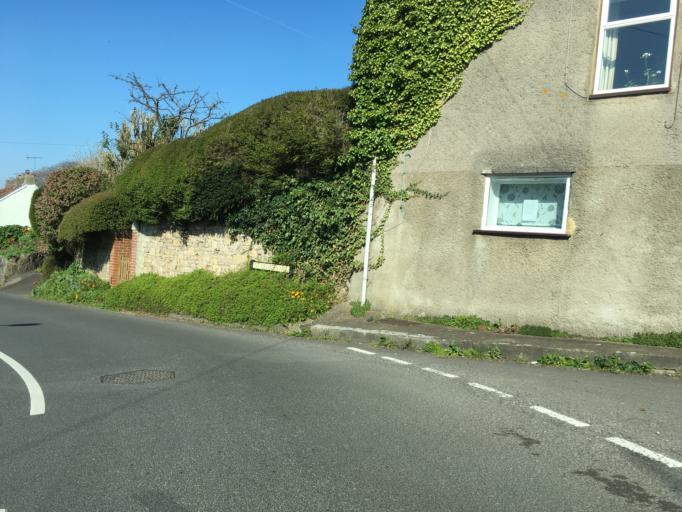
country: GB
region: England
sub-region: North Somerset
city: Easton-in-Gordano
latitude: 51.4747
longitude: -2.7006
